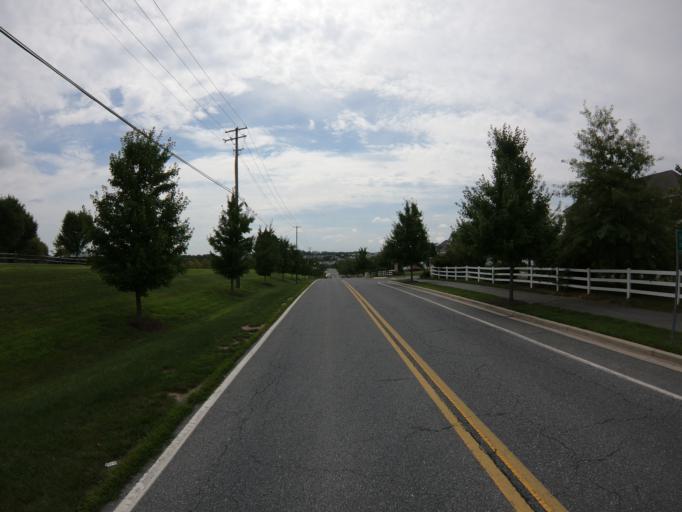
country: US
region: Maryland
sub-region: Montgomery County
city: Clarksburg
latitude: 39.2400
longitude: -77.2536
